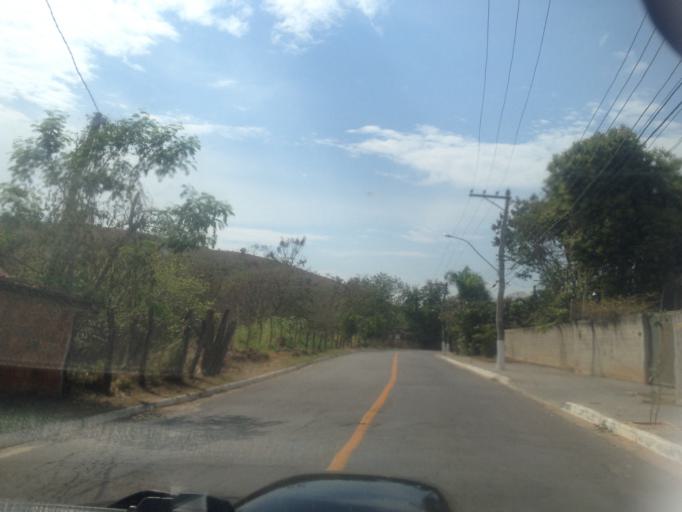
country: BR
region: Rio de Janeiro
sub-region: Tres Rios
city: Tres Rios
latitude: -22.1188
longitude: -43.1991
